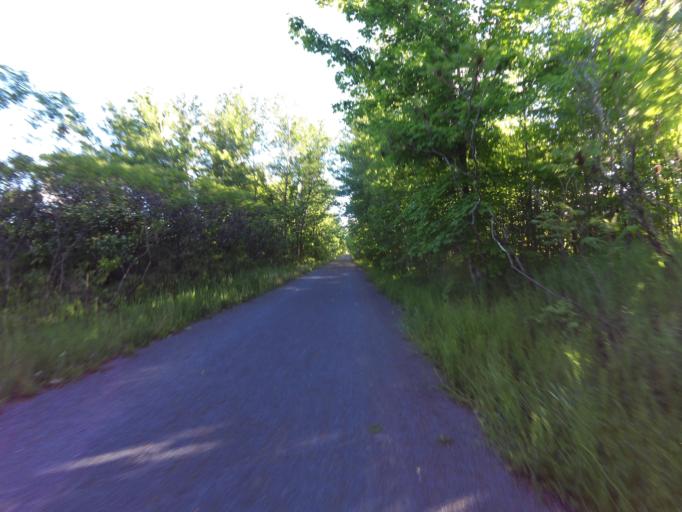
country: CA
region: Ontario
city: Bells Corners
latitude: 45.2714
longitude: -75.8999
